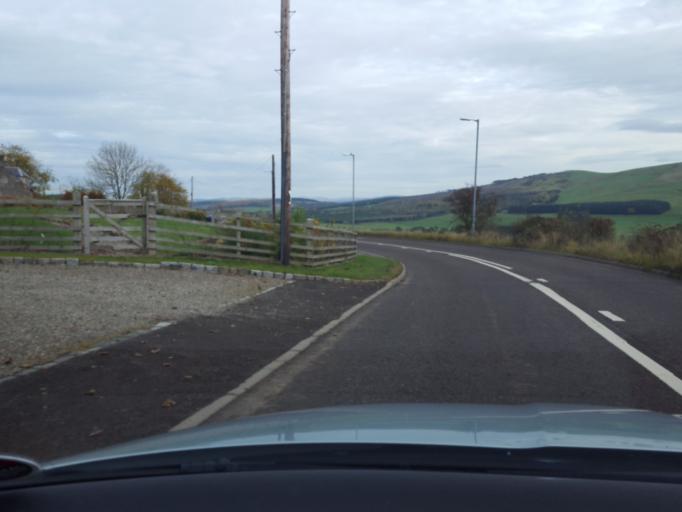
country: GB
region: Scotland
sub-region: South Lanarkshire
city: Biggar
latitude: 55.6771
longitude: -3.4888
